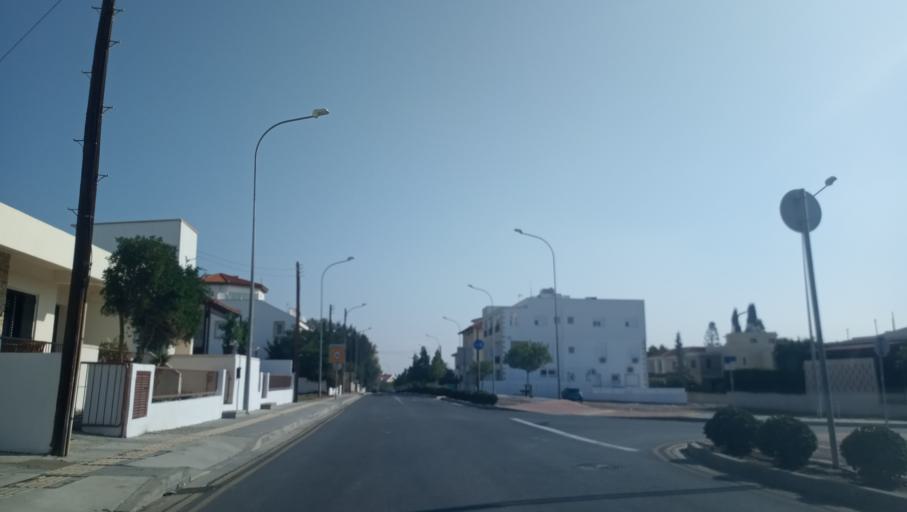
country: CY
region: Lefkosia
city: Nicosia
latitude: 35.1451
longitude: 33.3875
